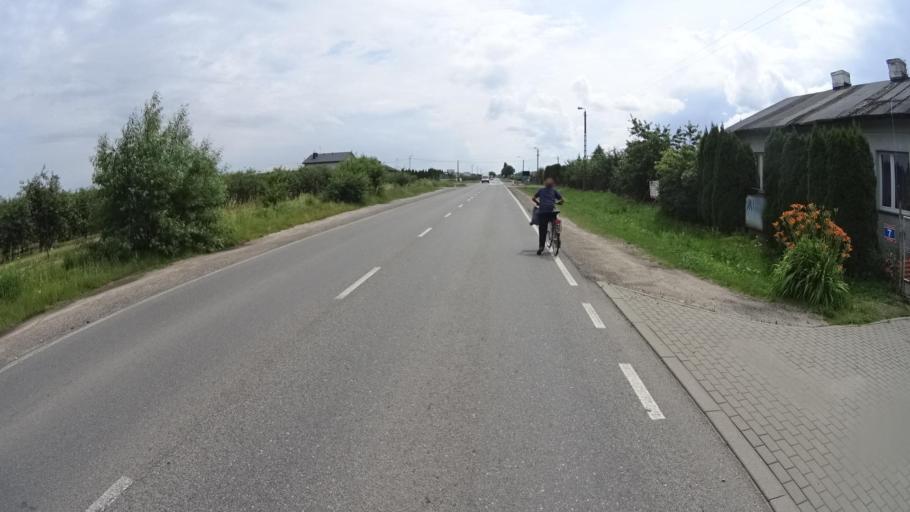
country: PL
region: Masovian Voivodeship
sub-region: Powiat grojecki
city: Grojec
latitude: 51.8896
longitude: 20.8627
